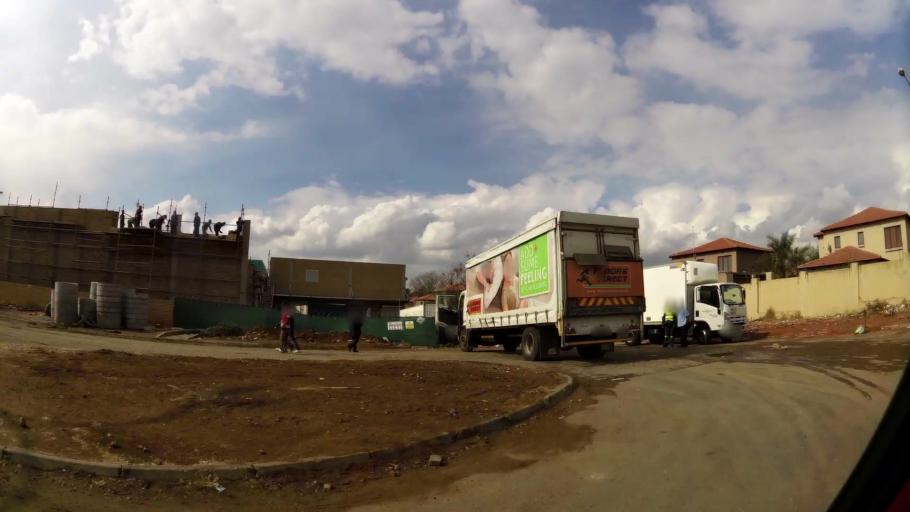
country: ZA
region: Gauteng
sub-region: Sedibeng District Municipality
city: Vanderbijlpark
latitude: -26.7353
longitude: 27.8377
